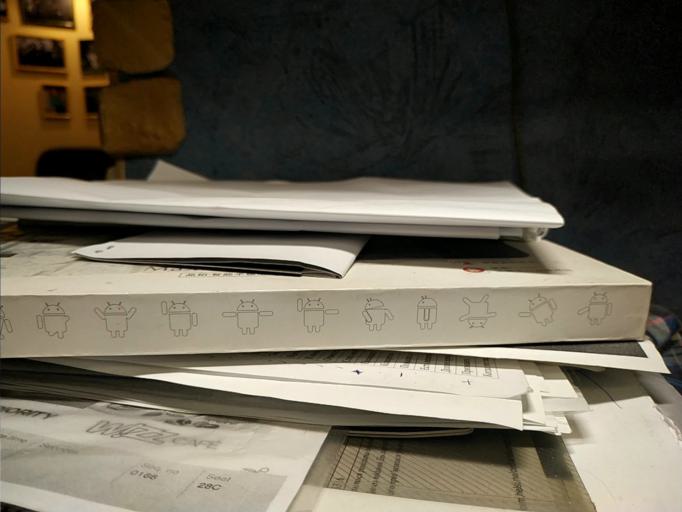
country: RU
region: Tverskaya
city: Zubtsov
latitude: 56.0840
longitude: 34.7808
